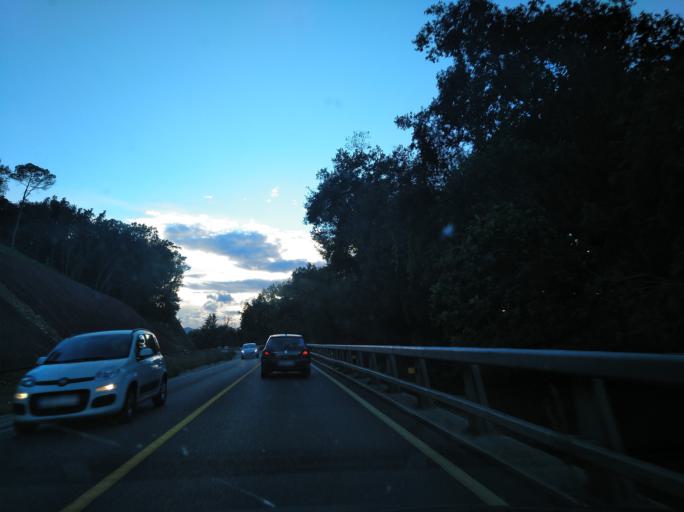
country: ES
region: Catalonia
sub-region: Provincia de Girona
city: Bescano
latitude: 41.9704
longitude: 2.7555
